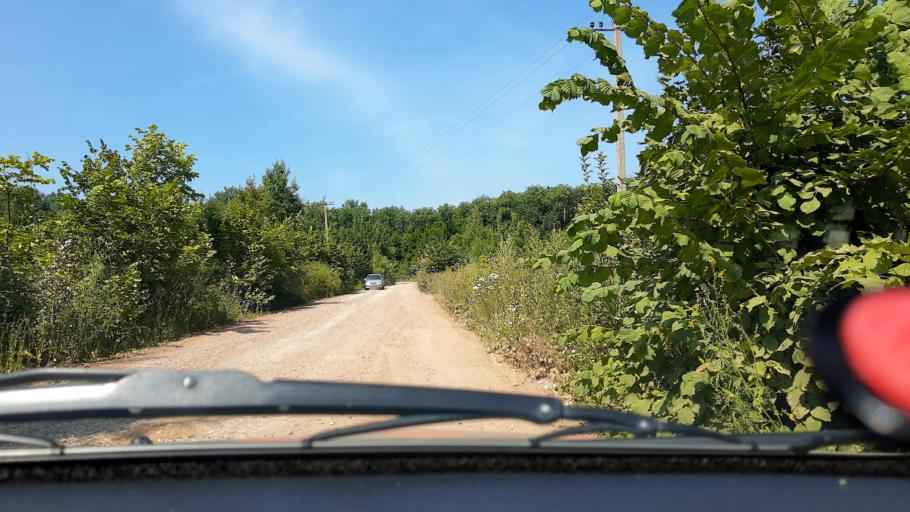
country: RU
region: Bashkortostan
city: Karmaskaly
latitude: 54.3886
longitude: 55.9015
